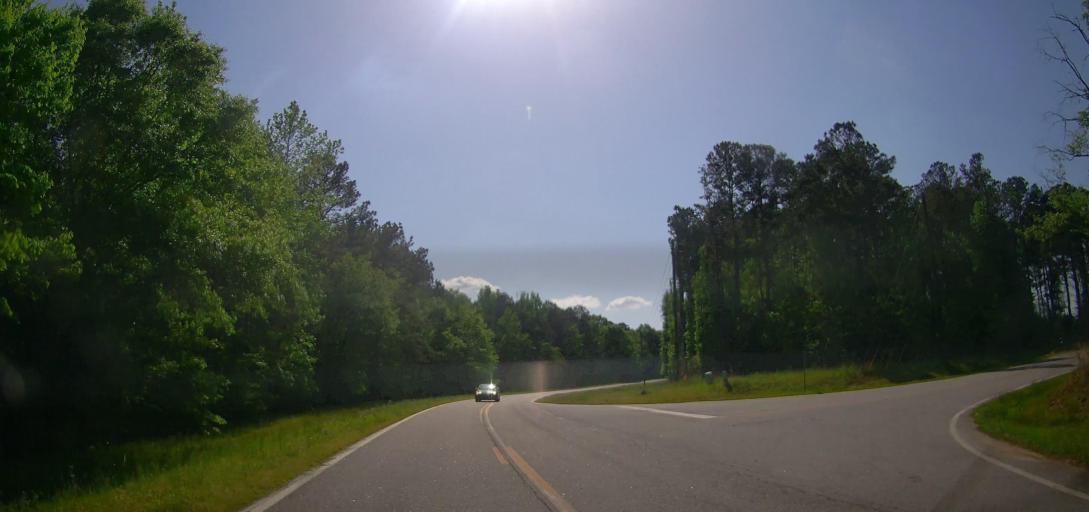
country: US
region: Georgia
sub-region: Morgan County
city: Madison
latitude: 33.5565
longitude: -83.4821
